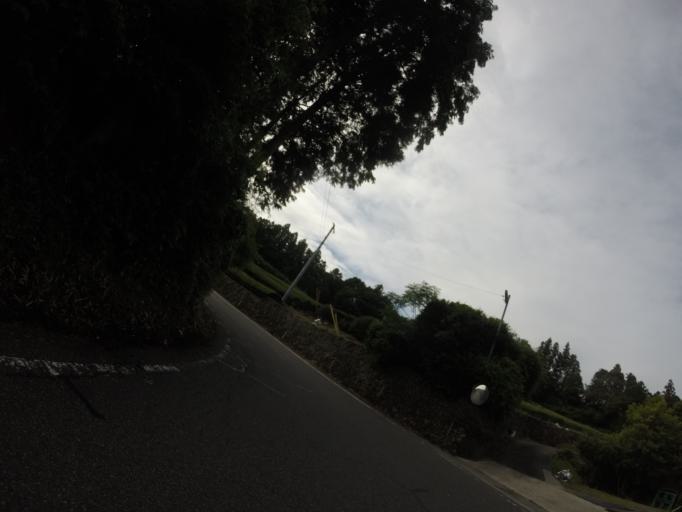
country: JP
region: Shizuoka
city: Kanaya
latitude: 34.7973
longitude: 138.1424
